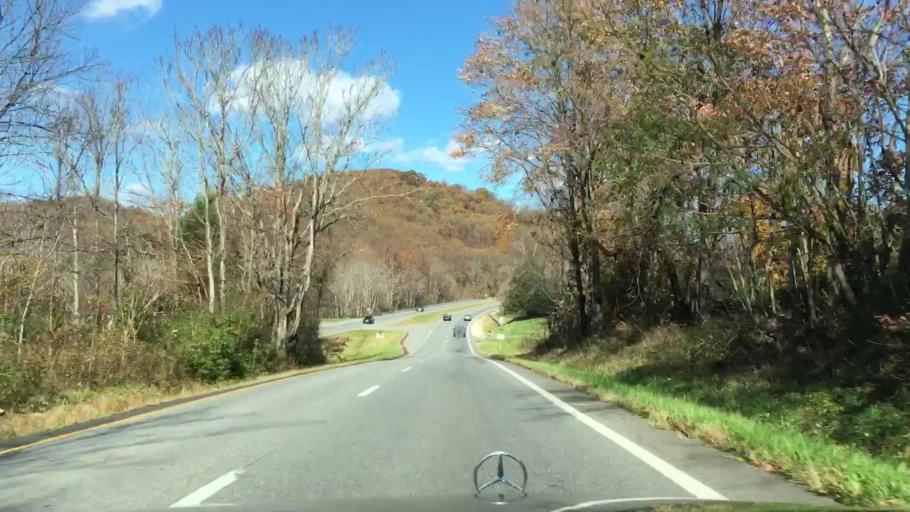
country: US
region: Virginia
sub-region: Nelson County
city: Nellysford
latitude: 37.8808
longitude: -78.7138
